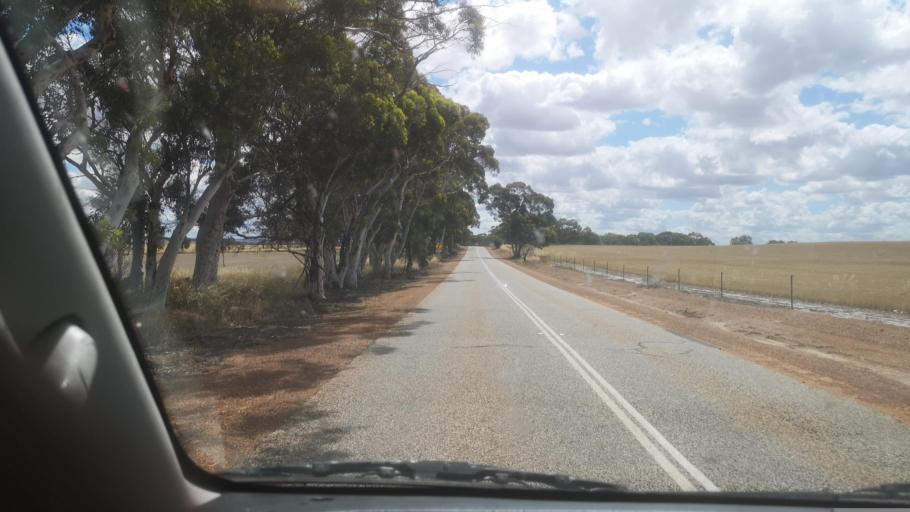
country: AU
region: Western Australia
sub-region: Beverley
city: Beverley
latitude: -31.9899
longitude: 117.1070
